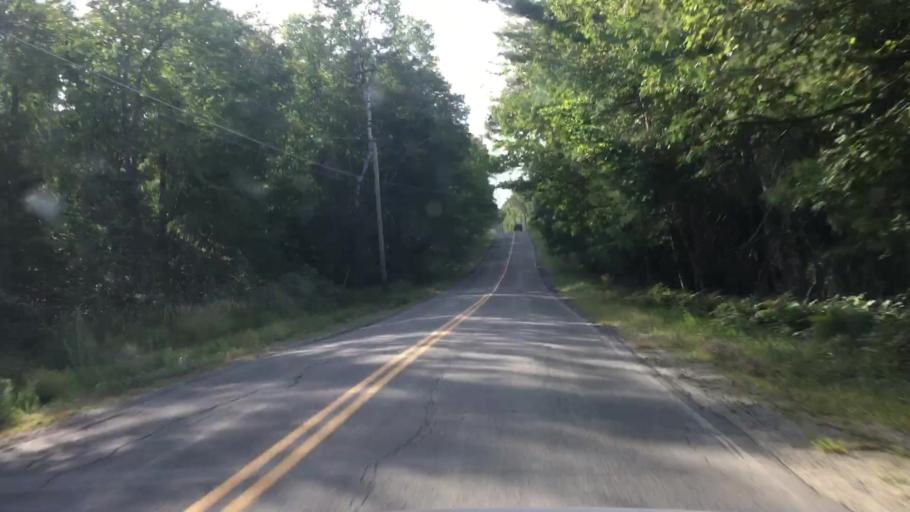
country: US
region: Maine
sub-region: Penobscot County
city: Enfield
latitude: 45.2382
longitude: -68.5508
